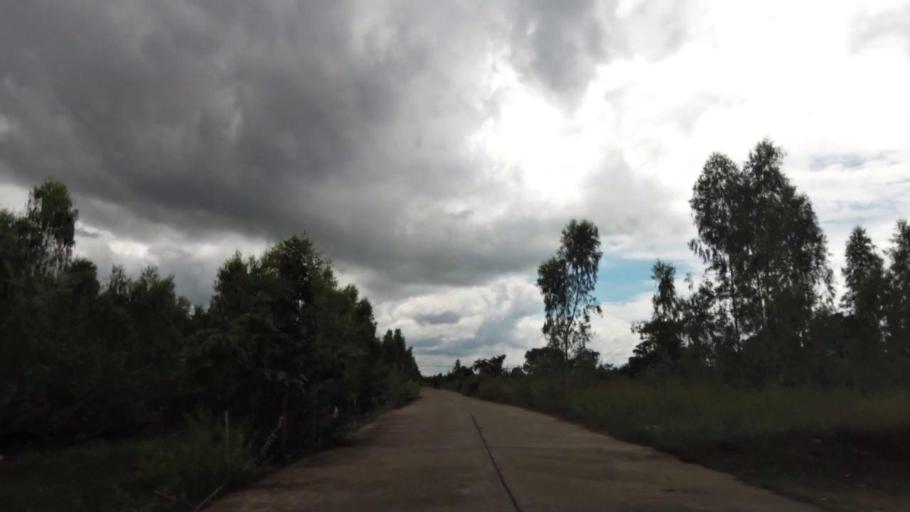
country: TH
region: Nakhon Sawan
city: Phai Sali
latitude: 15.6006
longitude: 100.6778
